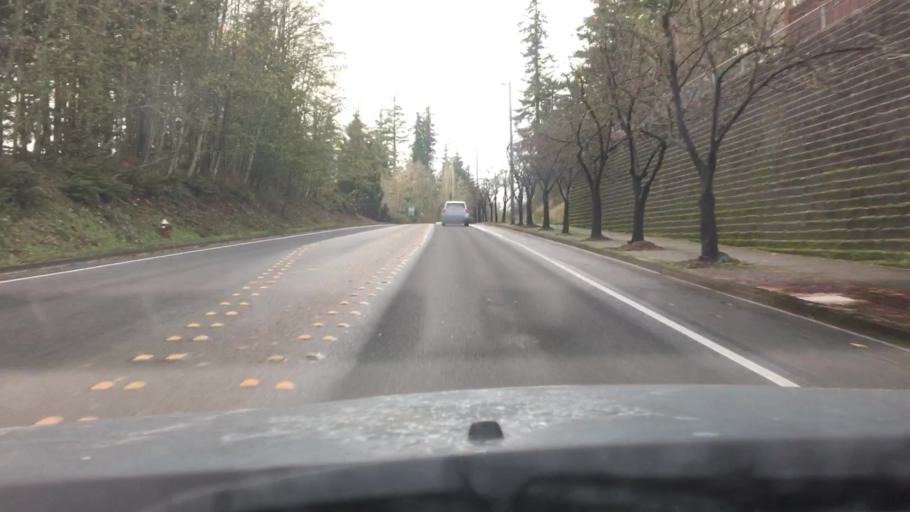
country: US
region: Washington
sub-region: Whatcom County
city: Geneva
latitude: 48.7720
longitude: -122.4219
